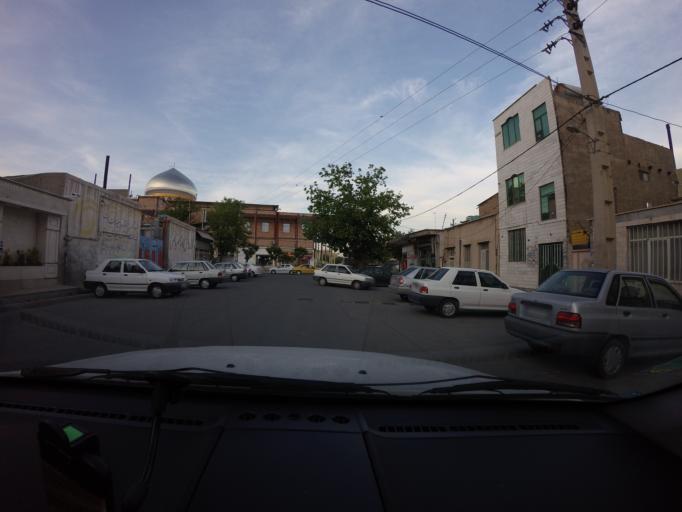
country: IR
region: Tehran
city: Eslamshahr
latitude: 35.5495
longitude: 51.2388
